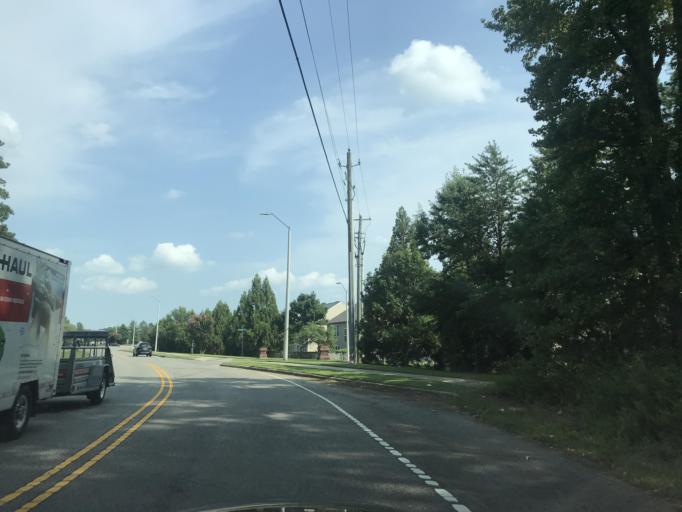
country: US
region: North Carolina
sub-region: Wake County
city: Morrisville
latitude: 35.8375
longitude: -78.8650
